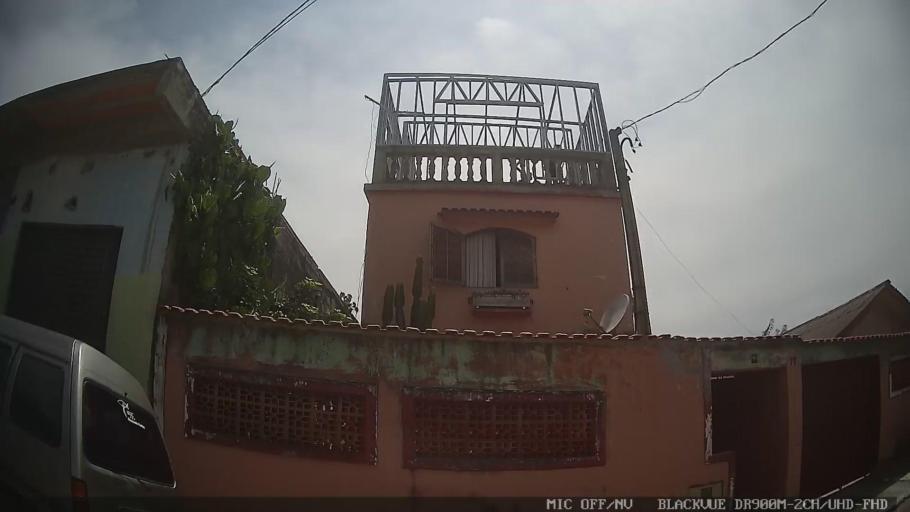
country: BR
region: Sao Paulo
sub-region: Ferraz De Vasconcelos
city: Ferraz de Vasconcelos
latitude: -23.5443
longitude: -46.3764
